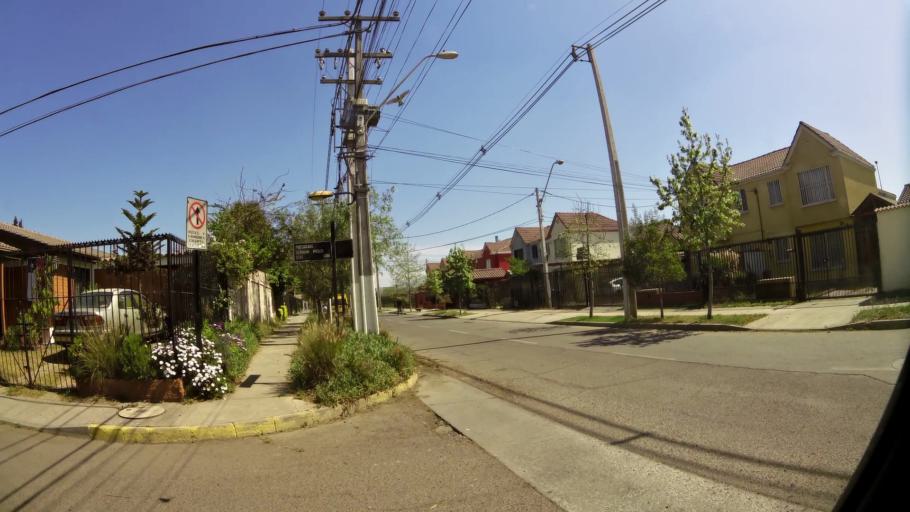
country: CL
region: Santiago Metropolitan
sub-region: Provincia de Santiago
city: Lo Prado
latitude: -33.4927
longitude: -70.7504
